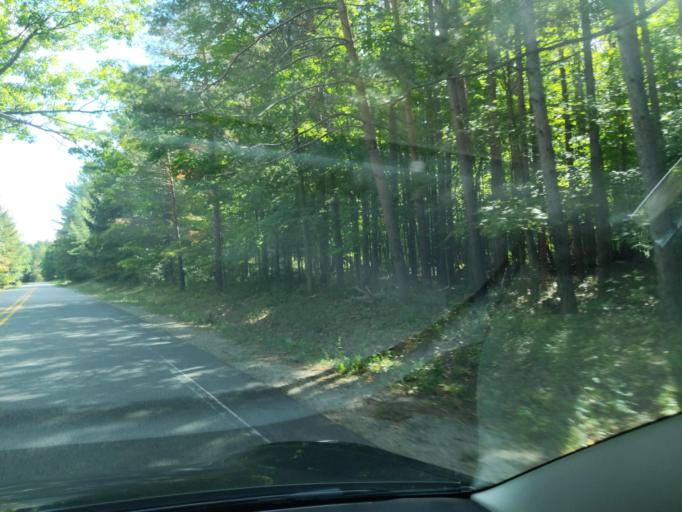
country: US
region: Michigan
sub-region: Antrim County
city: Bellaire
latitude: 45.0538
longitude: -85.3178
